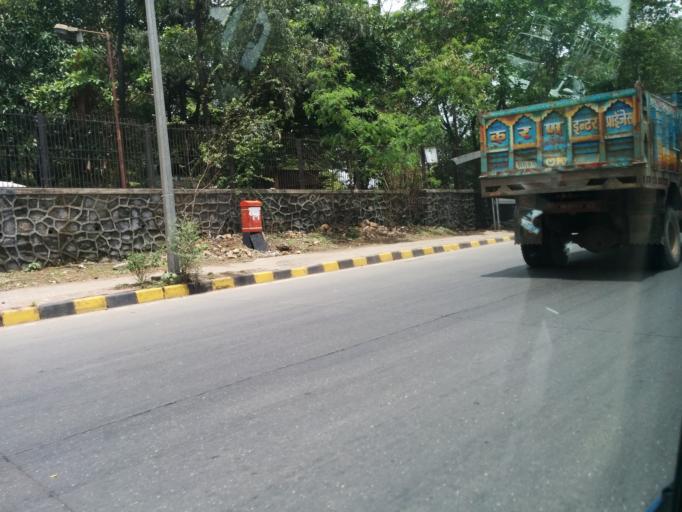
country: IN
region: Maharashtra
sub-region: Mumbai Suburban
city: Powai
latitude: 19.1339
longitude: 72.8746
